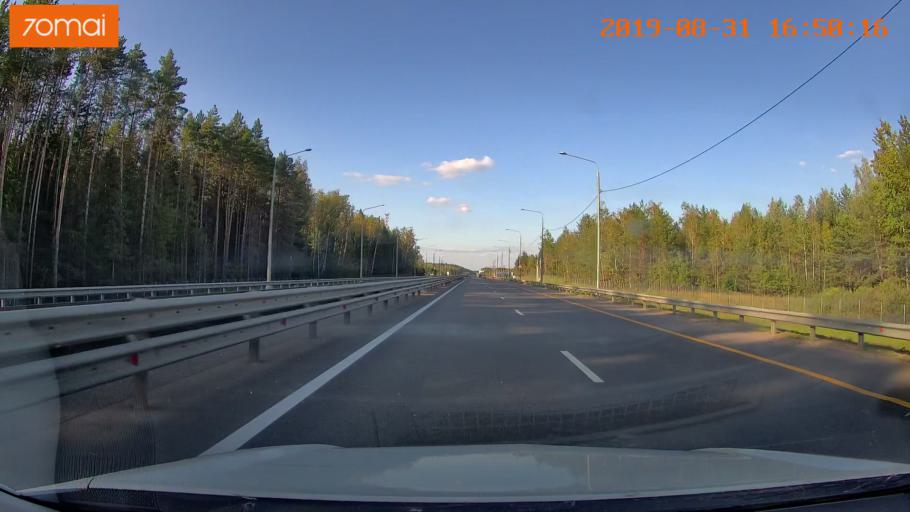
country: RU
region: Kaluga
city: Pyatovskiy
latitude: 54.7055
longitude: 36.1613
